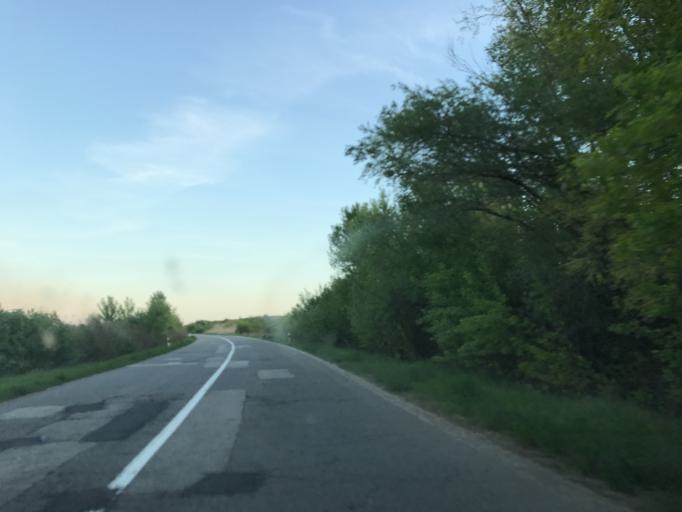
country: RO
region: Mehedinti
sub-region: Comuna Gogosu
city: Ostrovu Mare
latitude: 44.3929
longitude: 22.4652
